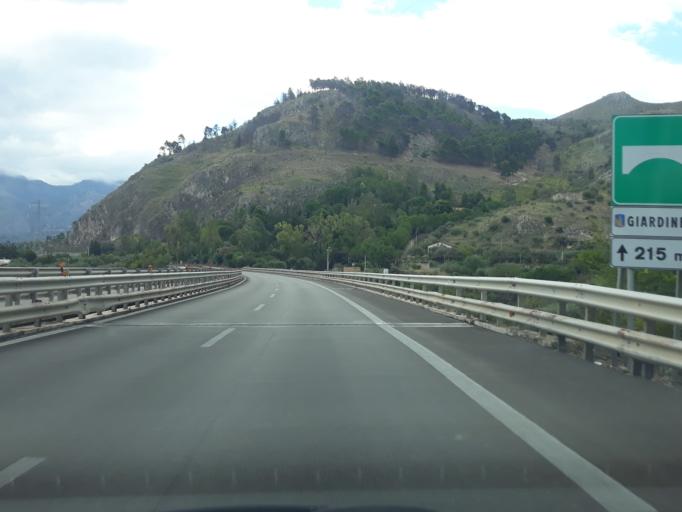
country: IT
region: Sicily
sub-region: Palermo
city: Trabia
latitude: 37.9870
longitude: 13.6559
